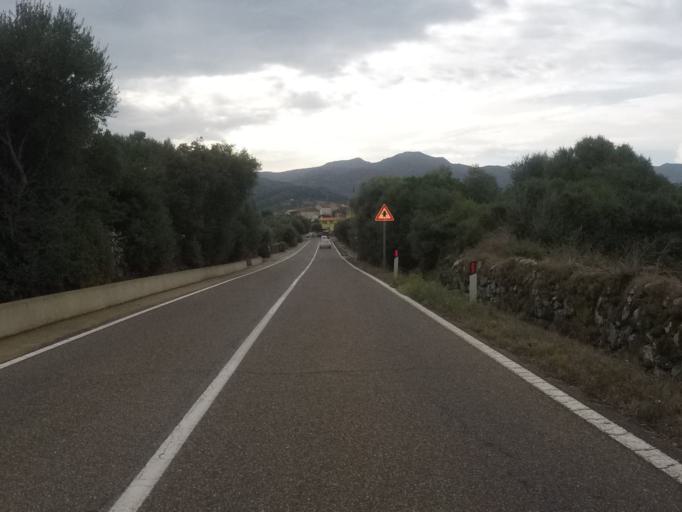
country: IT
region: Sardinia
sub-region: Provincia di Oristano
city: Sennariolo
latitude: 40.2142
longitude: 8.5535
